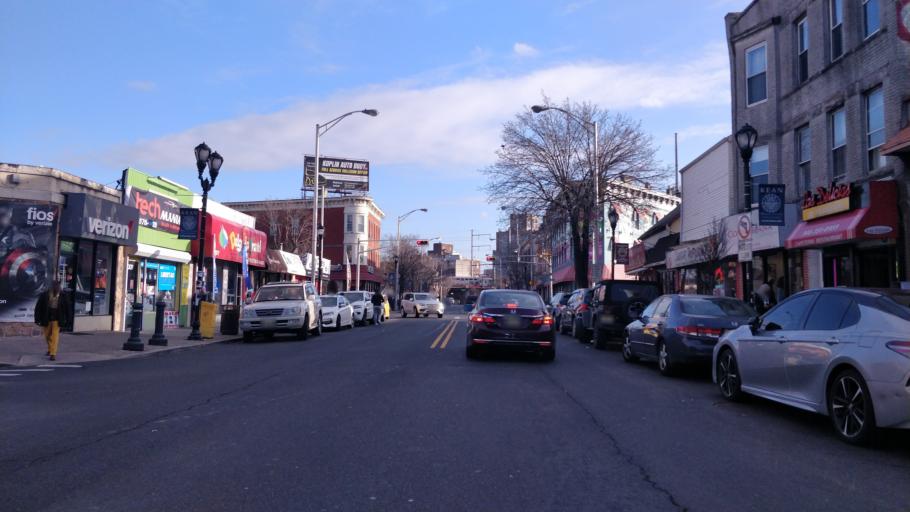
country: US
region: New Jersey
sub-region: Union County
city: Elizabeth
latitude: 40.6689
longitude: -74.2177
